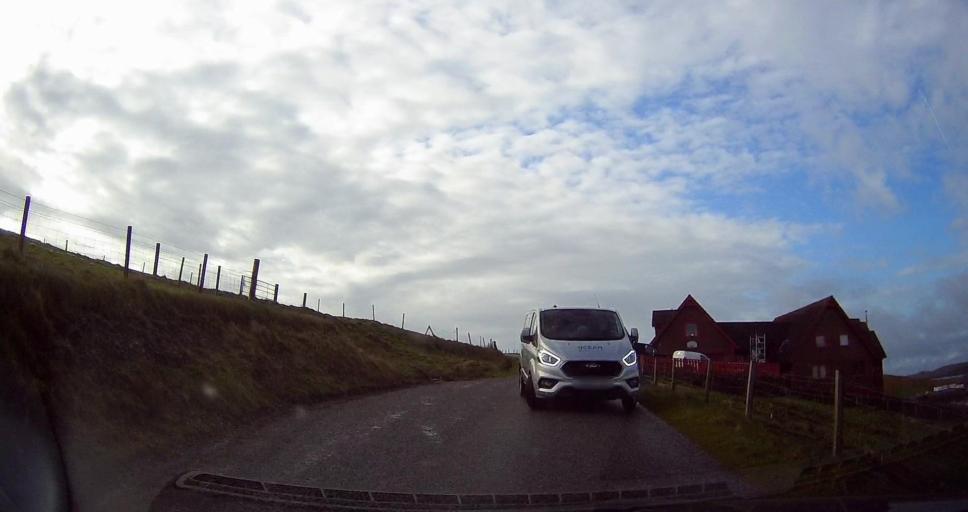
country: GB
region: Scotland
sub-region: Shetland Islands
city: Sandwick
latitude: 60.0447
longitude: -1.2062
